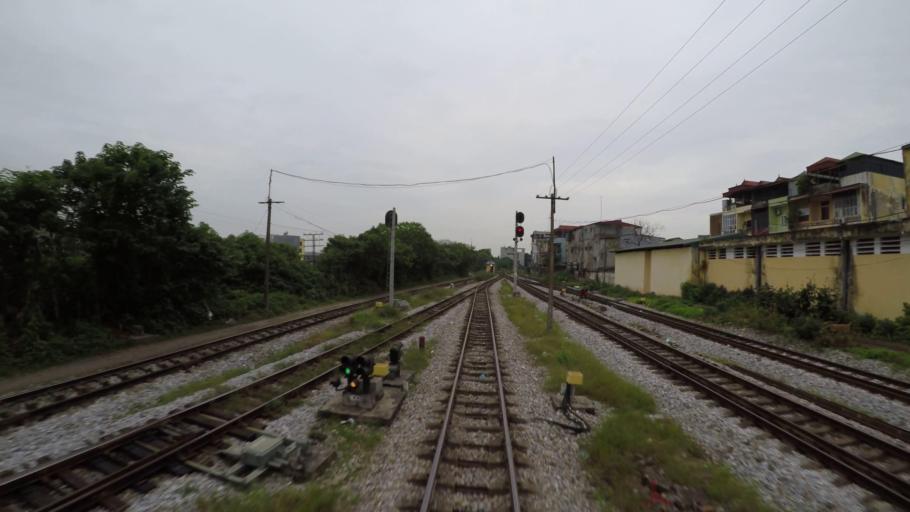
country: VN
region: Ha Noi
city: Trau Quy
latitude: 21.0242
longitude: 105.9292
